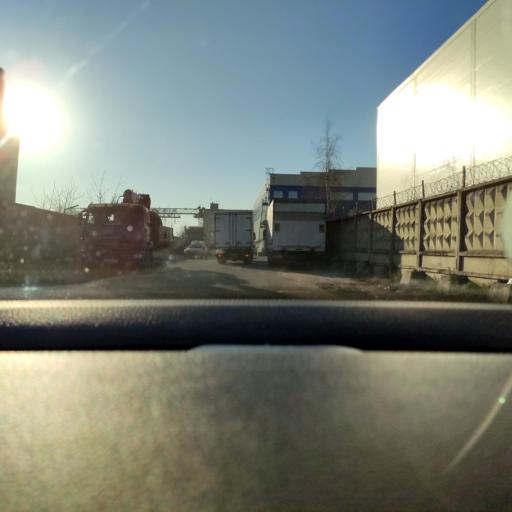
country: RU
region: Moskovskaya
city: Kotel'niki
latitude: 55.6304
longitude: 37.8233
